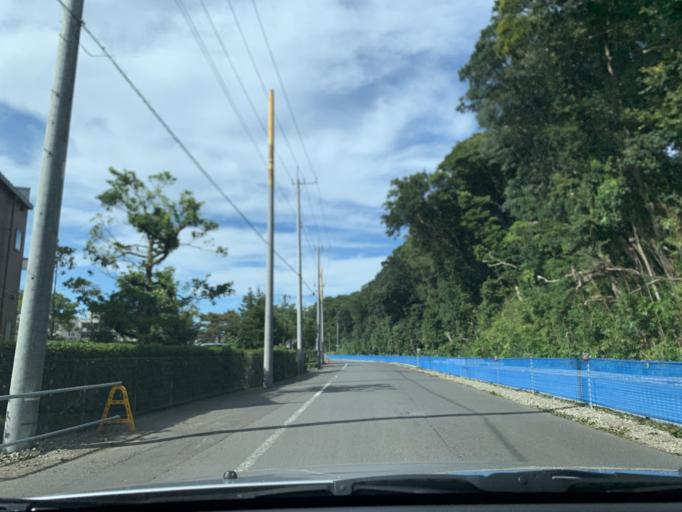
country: JP
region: Chiba
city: Nagareyama
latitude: 35.8936
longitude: 139.8970
